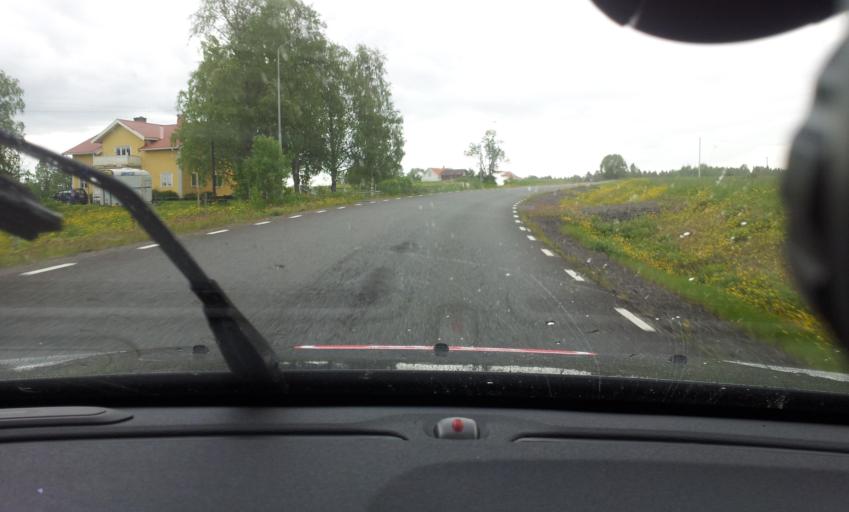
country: SE
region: Jaemtland
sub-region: OEstersunds Kommun
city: Brunflo
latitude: 63.1845
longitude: 14.9133
